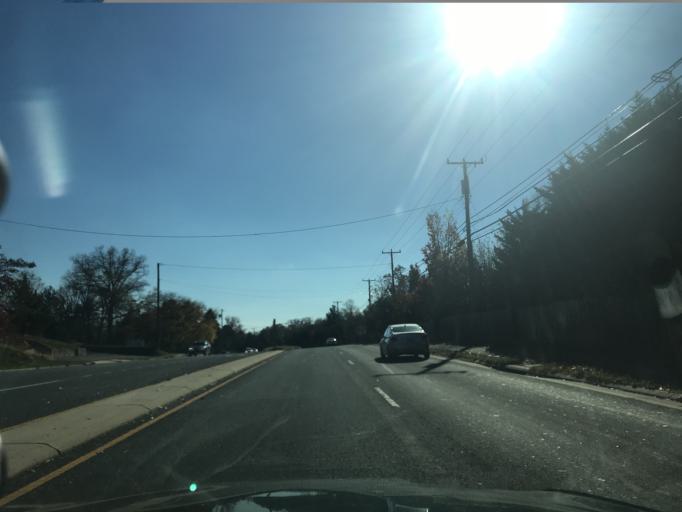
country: US
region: Virginia
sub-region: Fairfax County
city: Greenbriar
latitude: 38.8951
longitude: -77.3804
